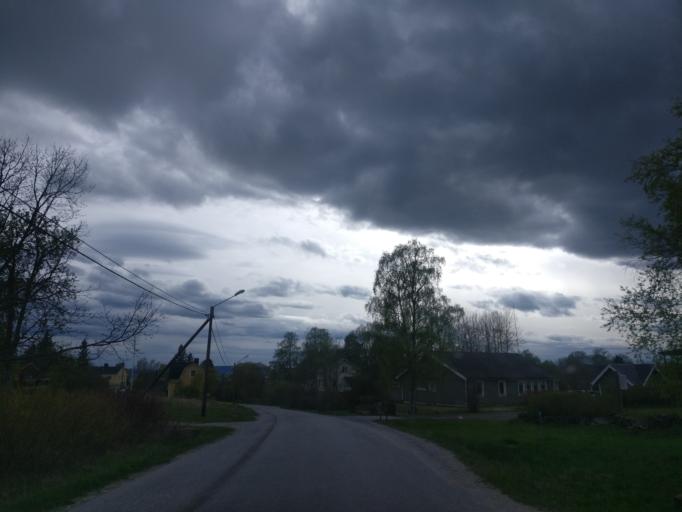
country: SE
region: Vaesternorrland
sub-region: Timra Kommun
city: Soraker
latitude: 62.5119
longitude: 17.5115
